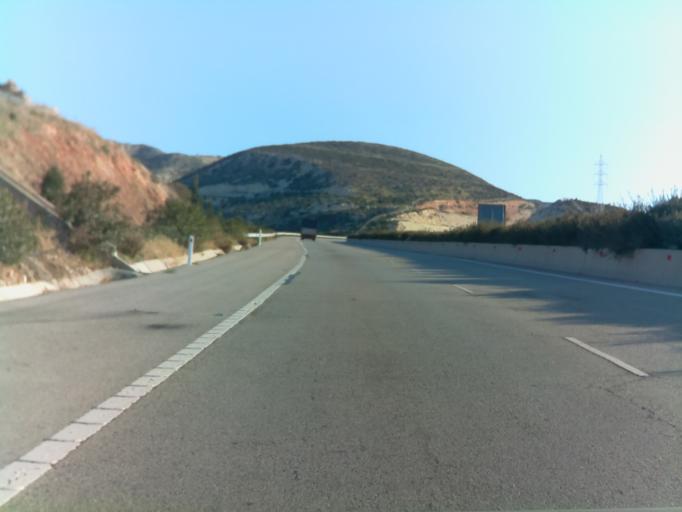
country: CY
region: Limassol
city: Pissouri
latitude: 34.6702
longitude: 32.6251
